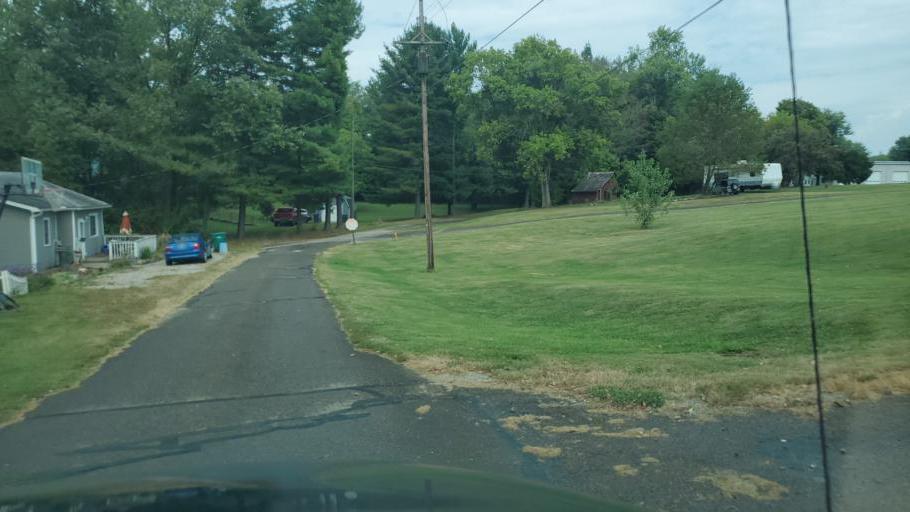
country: US
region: Ohio
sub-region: Perry County
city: Somerset
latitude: 39.9515
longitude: -82.2169
